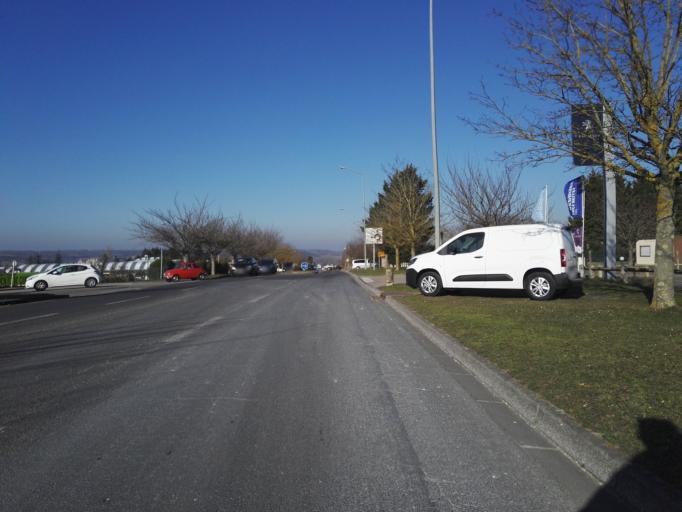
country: FR
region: Haute-Normandie
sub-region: Departement de l'Eure
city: Pacy-sur-Eure
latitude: 49.0107
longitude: 1.3967
